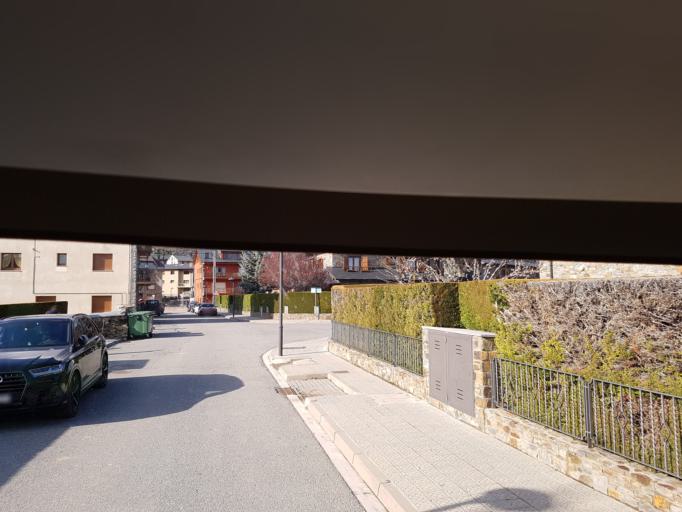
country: ES
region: Catalonia
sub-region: Provincia de Girona
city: Llivia
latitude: 42.4619
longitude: 1.9798
